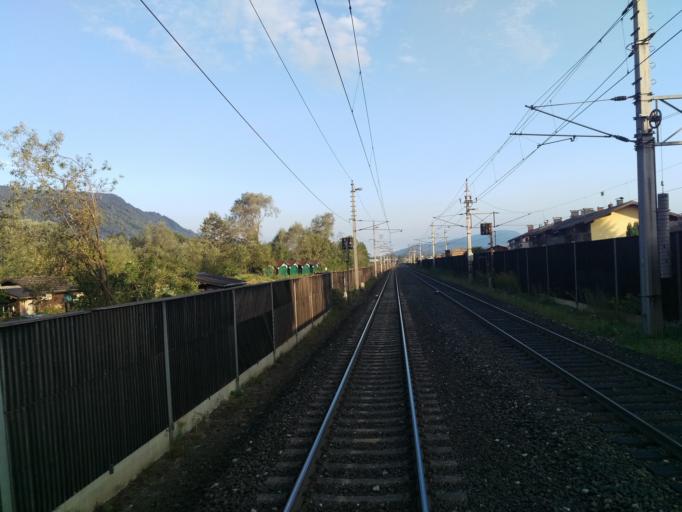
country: AT
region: Salzburg
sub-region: Politischer Bezirk Hallein
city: Kuchl
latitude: 47.6287
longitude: 13.1403
